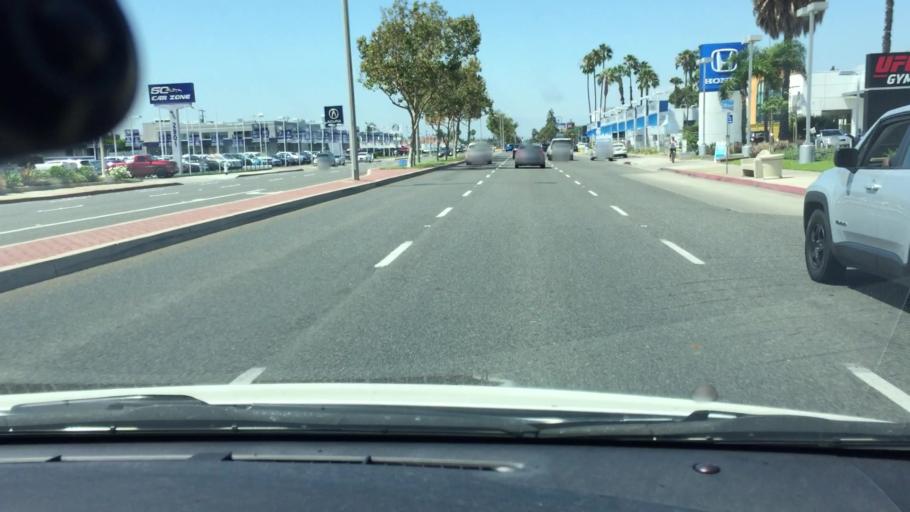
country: US
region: California
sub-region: Orange County
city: Costa Mesa
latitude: 33.6756
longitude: -117.9192
